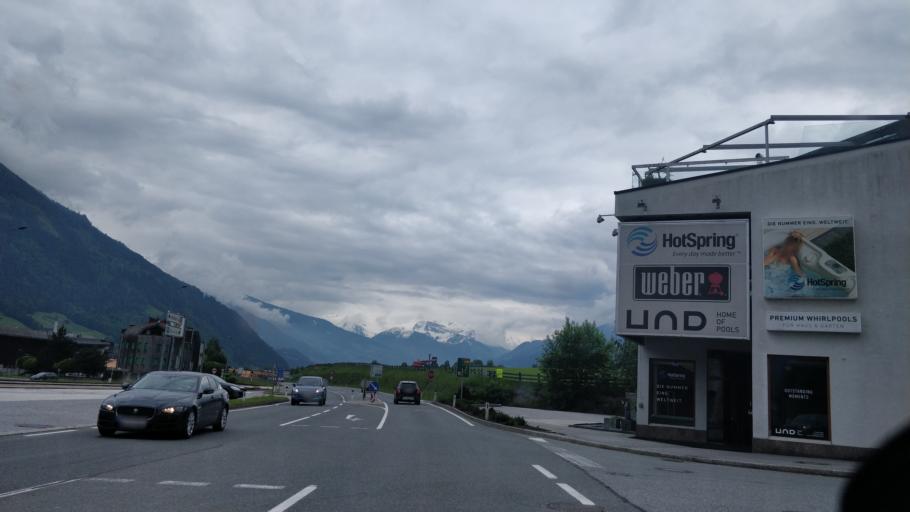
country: AT
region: Tyrol
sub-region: Politischer Bezirk Schwaz
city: Fugen
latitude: 47.3446
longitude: 11.8528
